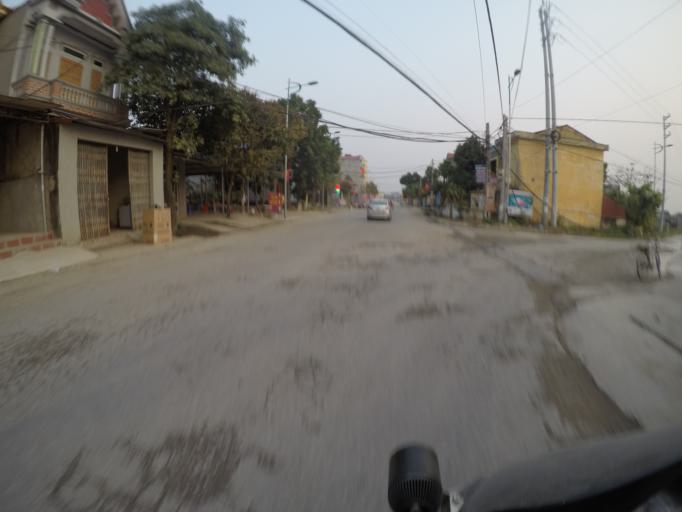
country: VN
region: Vinh Phuc
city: Trai Ngau
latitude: 21.4581
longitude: 105.5674
